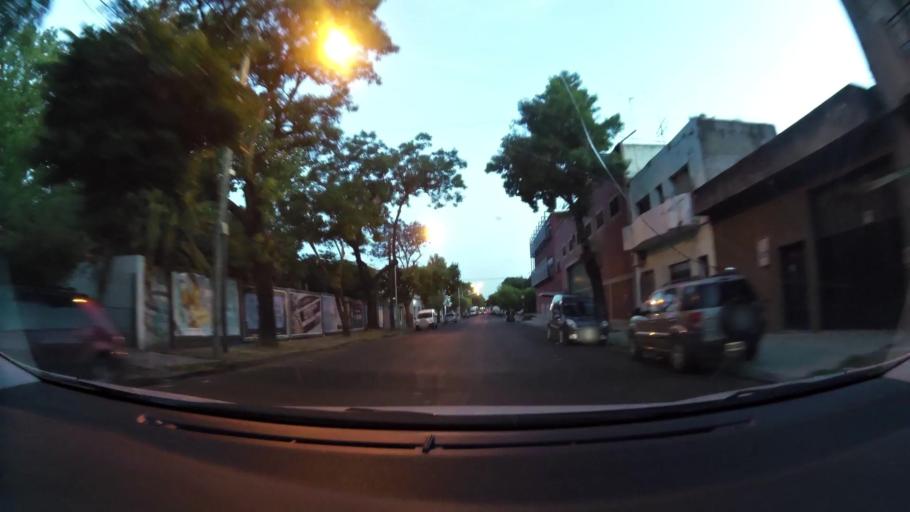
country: AR
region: Buenos Aires F.D.
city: Villa Lugano
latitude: -34.6912
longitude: -58.4672
